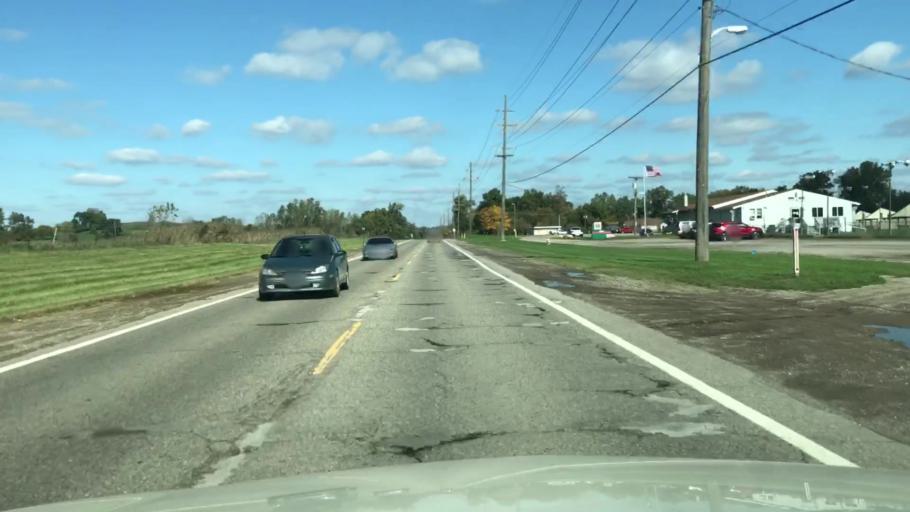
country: US
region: Michigan
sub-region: Oakland County
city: Rochester
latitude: 42.6561
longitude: -83.0929
